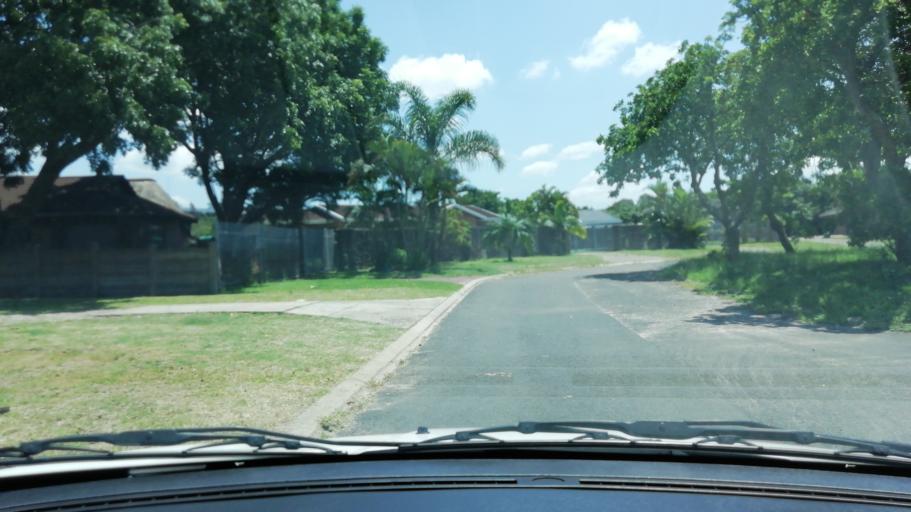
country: ZA
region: KwaZulu-Natal
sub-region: uThungulu District Municipality
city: Richards Bay
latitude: -28.7339
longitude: 32.0512
